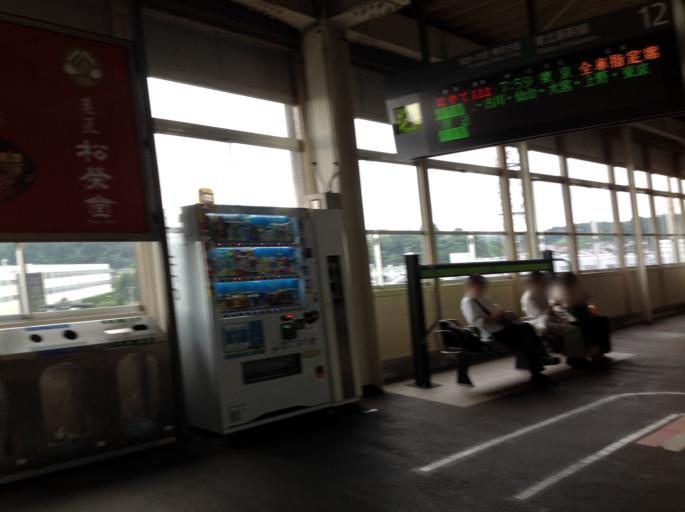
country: JP
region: Iwate
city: Ichinoseki
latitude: 38.9261
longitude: 141.1392
